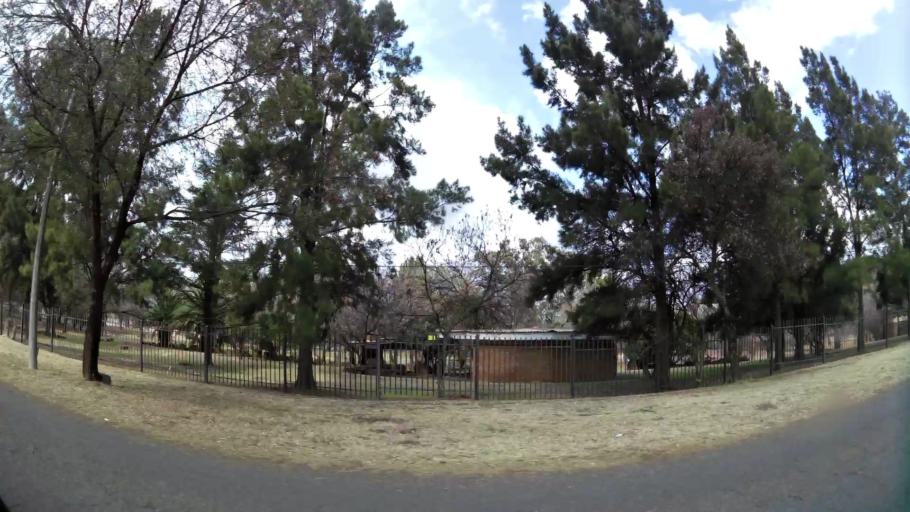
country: ZA
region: Gauteng
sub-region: Sedibeng District Municipality
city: Vanderbijlpark
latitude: -26.7487
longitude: 27.8330
